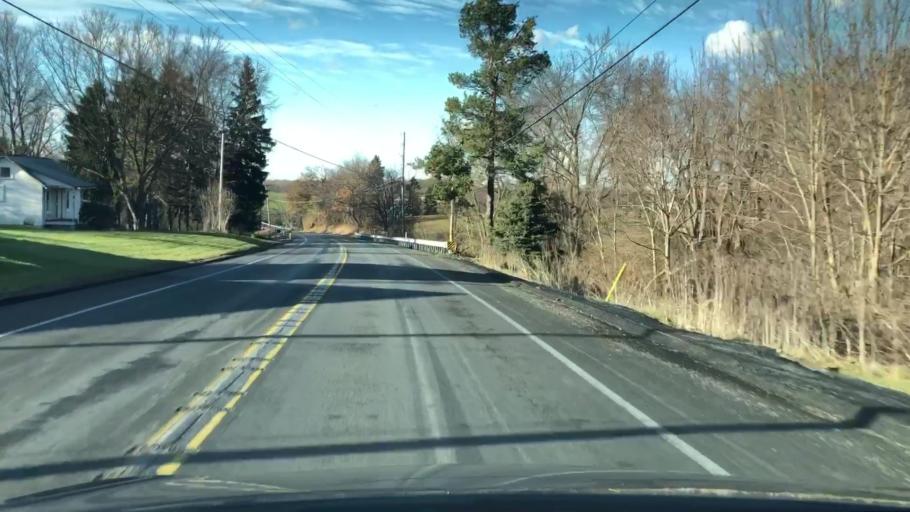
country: US
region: Pennsylvania
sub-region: Butler County
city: Saxonburg
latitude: 40.7852
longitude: -79.7999
